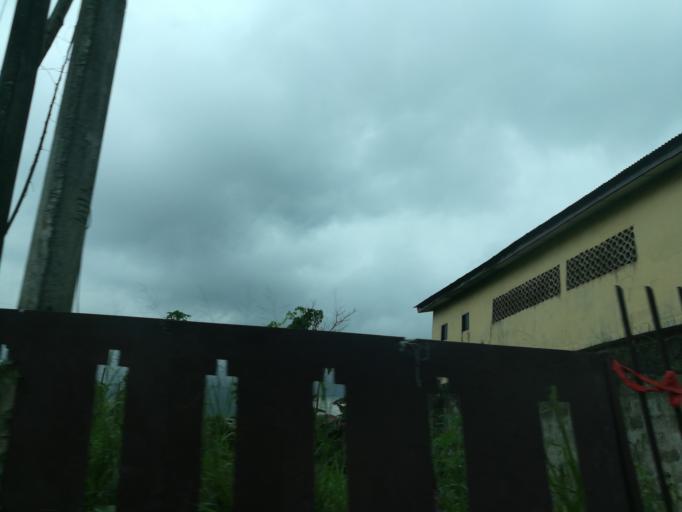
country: NG
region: Rivers
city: Port Harcourt
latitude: 4.8395
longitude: 7.0309
